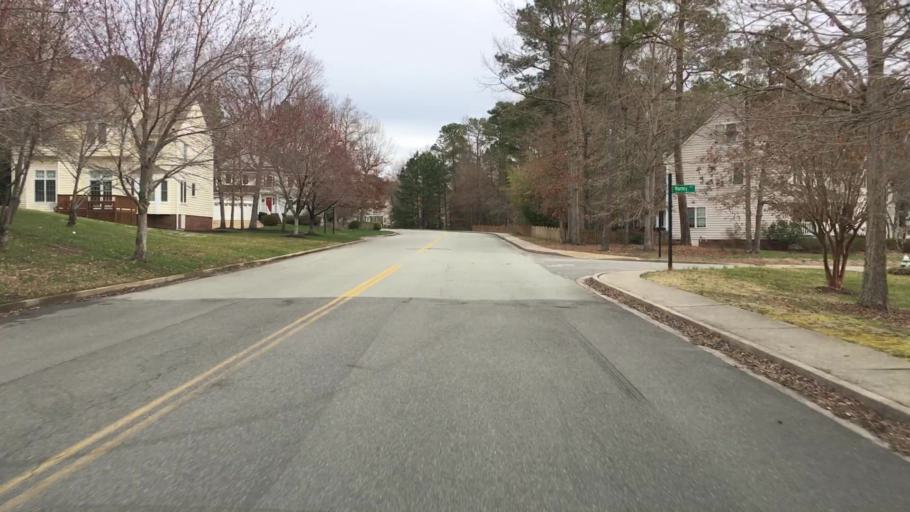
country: US
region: Virginia
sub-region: Henrico County
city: Short Pump
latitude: 37.6498
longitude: -77.5730
